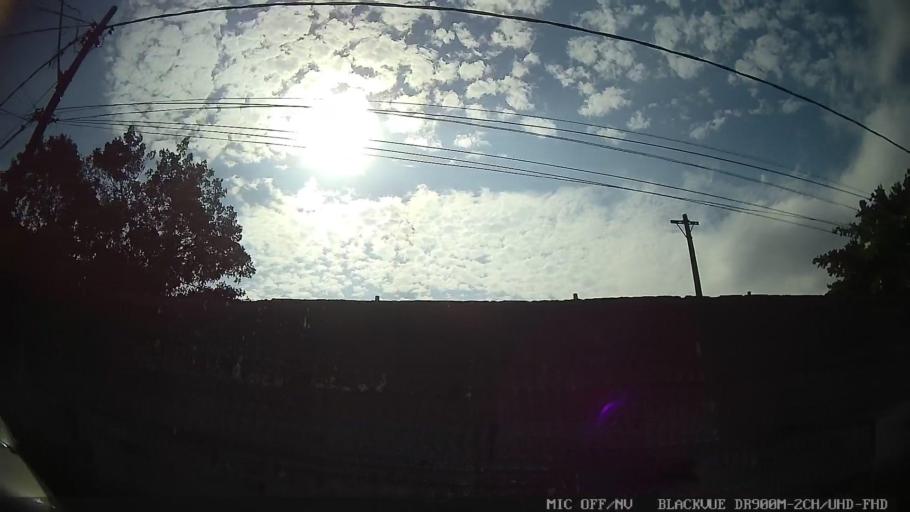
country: BR
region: Sao Paulo
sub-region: Santos
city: Santos
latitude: -23.9511
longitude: -46.2996
